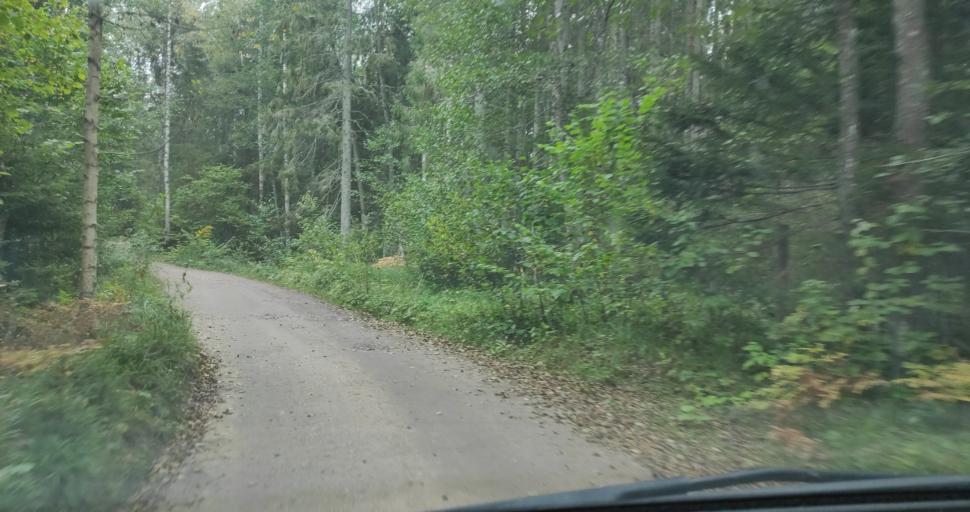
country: LV
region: Kuldigas Rajons
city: Kuldiga
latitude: 57.2389
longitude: 22.0960
